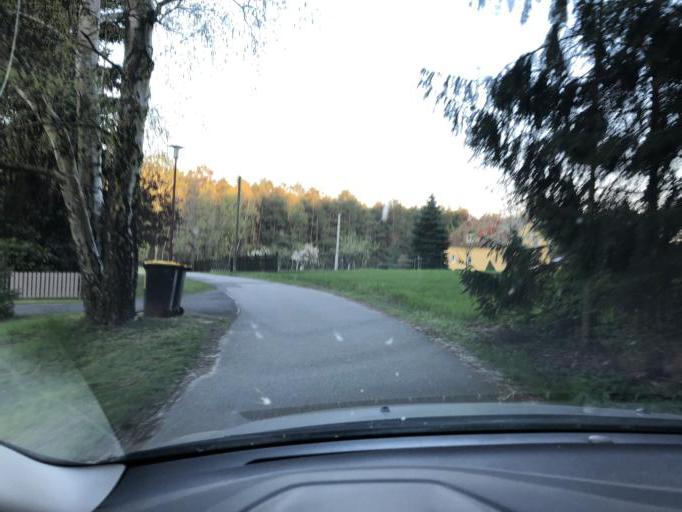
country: DE
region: Saxony
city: Gross Duben
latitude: 51.5750
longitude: 14.5511
